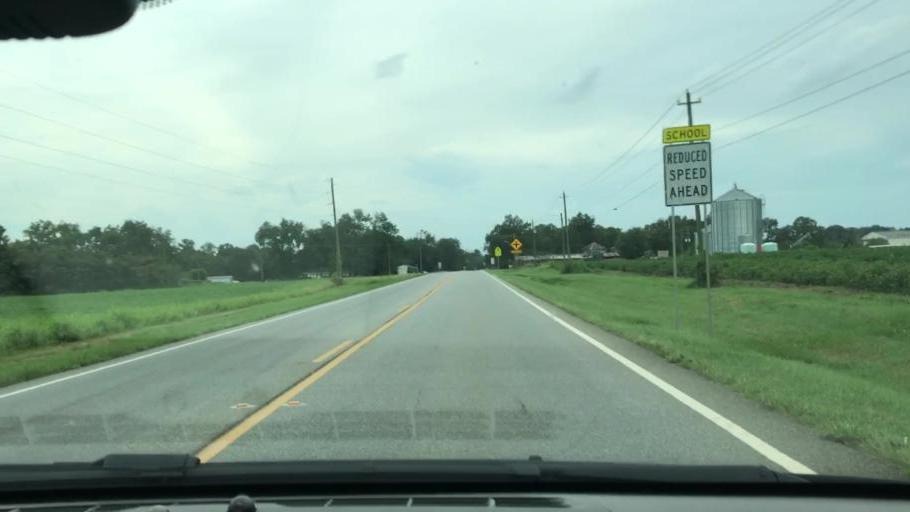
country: US
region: Georgia
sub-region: Early County
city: Blakely
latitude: 31.3772
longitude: -84.9575
